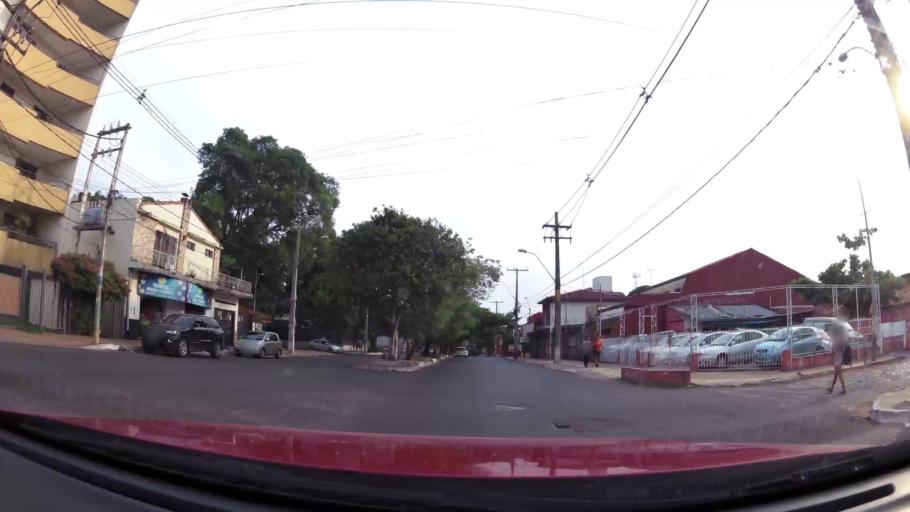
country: PY
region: Asuncion
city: Asuncion
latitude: -25.3061
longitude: -57.6081
